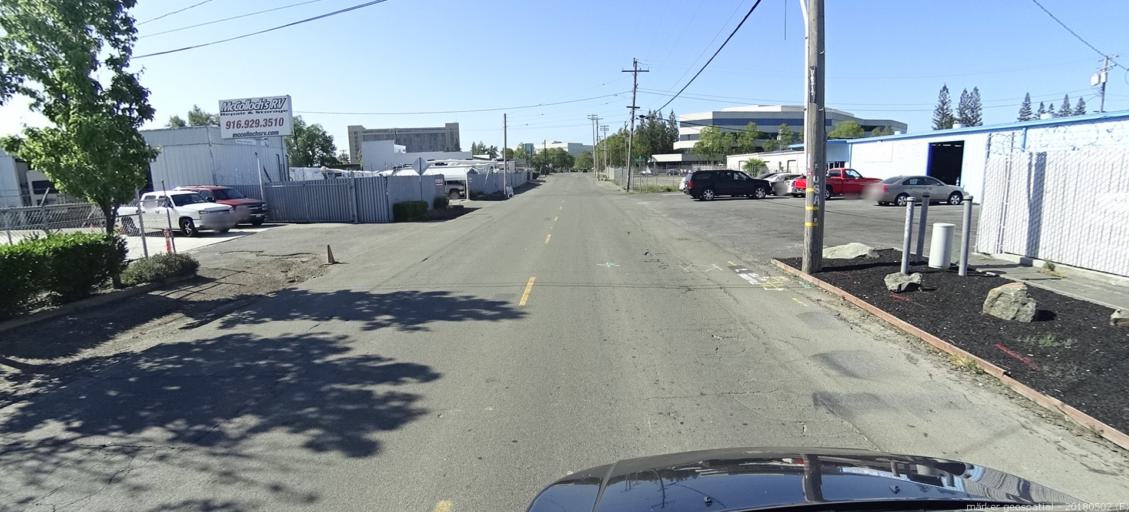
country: US
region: California
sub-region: Sacramento County
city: Arden-Arcade
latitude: 38.6099
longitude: -121.4348
